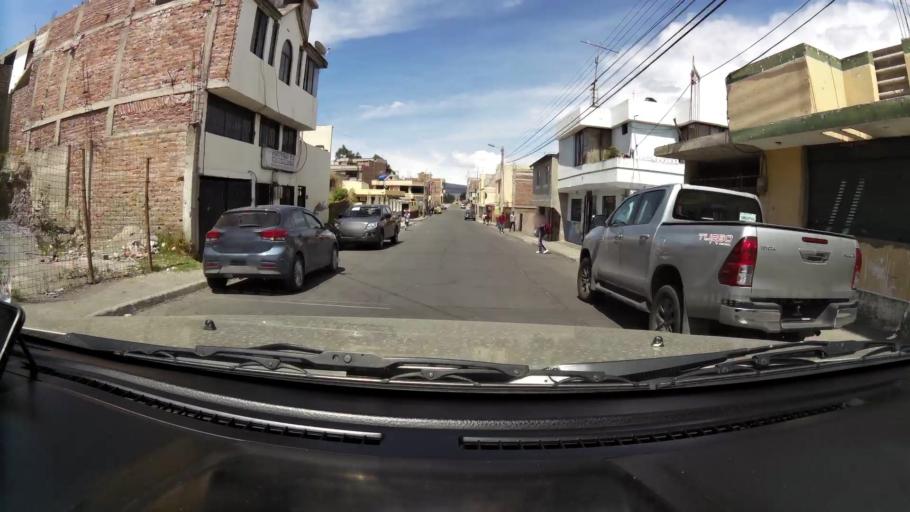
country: EC
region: Chimborazo
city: Riobamba
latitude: -1.6587
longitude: -78.6441
